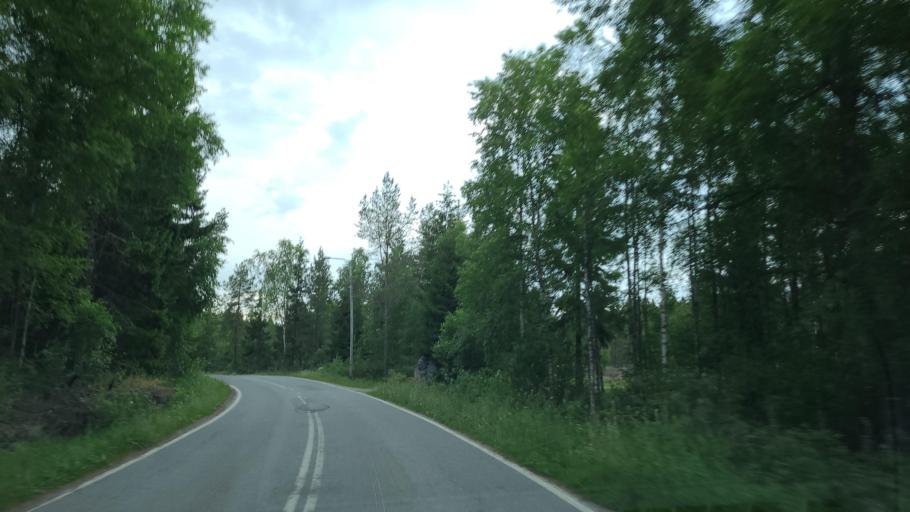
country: FI
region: Ostrobothnia
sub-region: Vaasa
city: Replot
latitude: 63.1741
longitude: 21.2776
